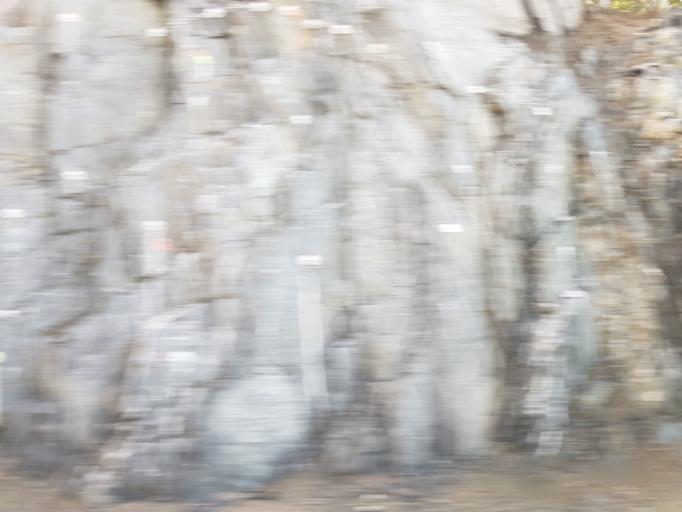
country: NO
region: Sor-Trondelag
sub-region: Trondheim
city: Trondheim
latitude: 63.6729
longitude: 10.2429
